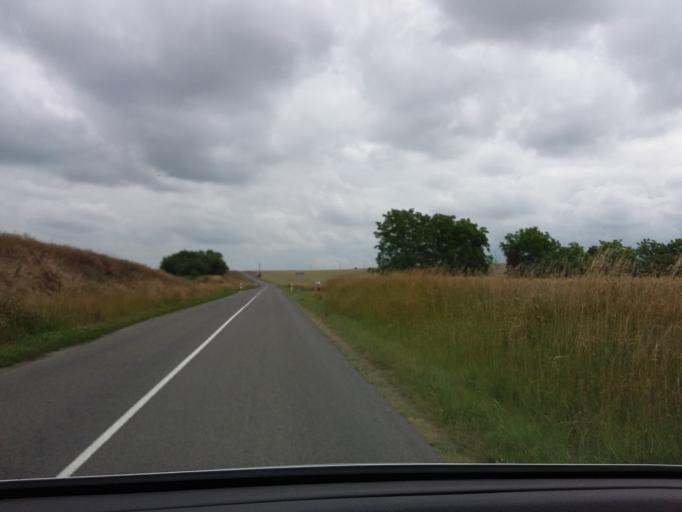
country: FR
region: Champagne-Ardenne
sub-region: Departement de la Marne
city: Jonchery-sur-Vesle
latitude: 49.3889
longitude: 3.7670
